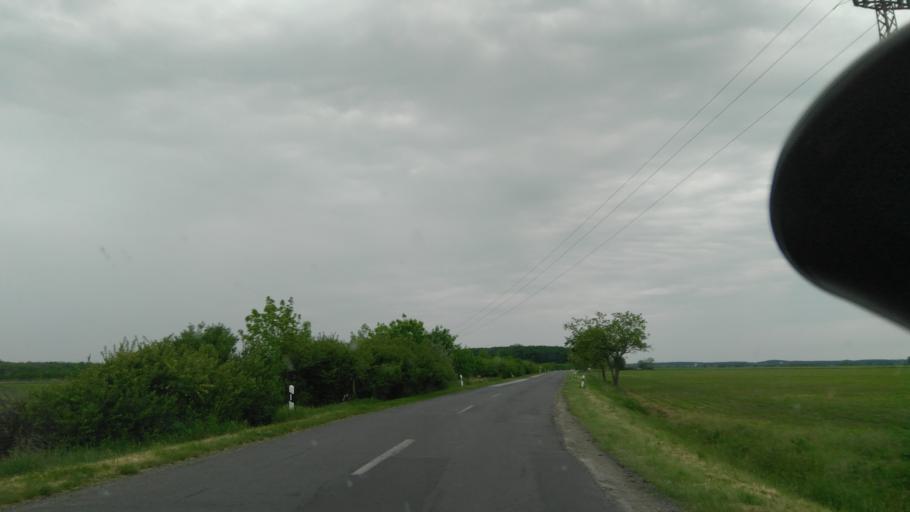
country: HU
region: Bekes
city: Doboz
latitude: 46.7269
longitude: 21.2801
